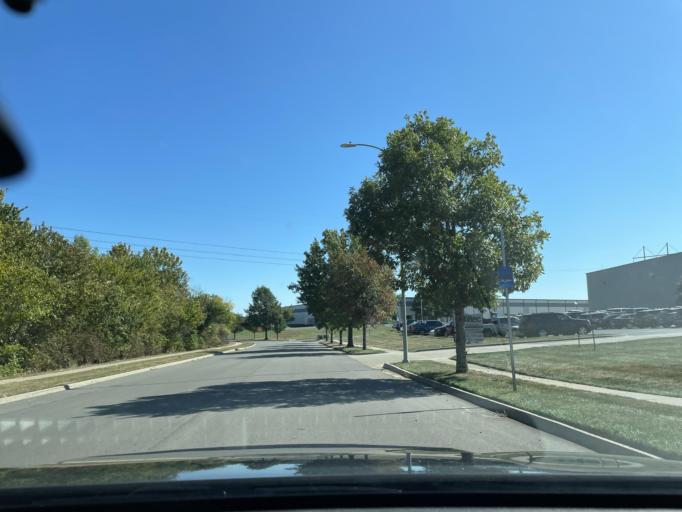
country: US
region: Missouri
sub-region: Buchanan County
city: Saint Joseph
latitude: 39.7513
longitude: -94.7634
